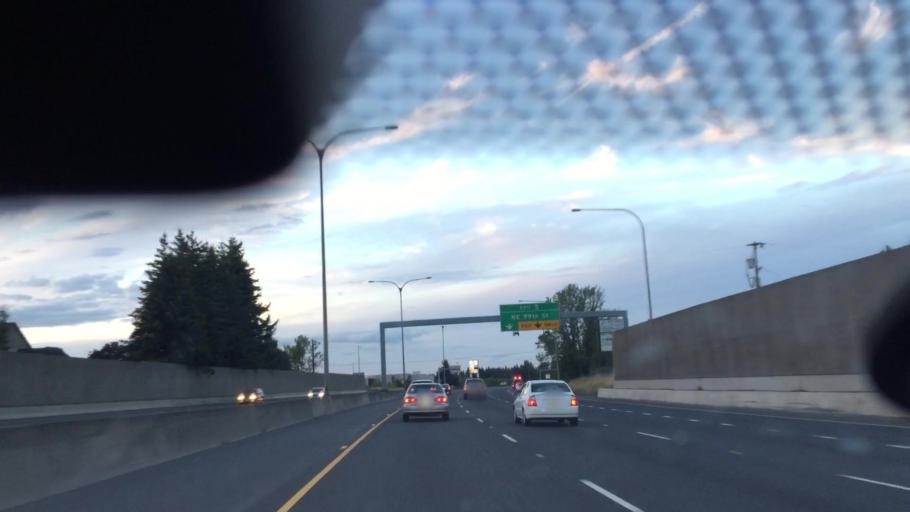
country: US
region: Washington
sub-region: Clark County
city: Hazel Dell
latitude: 45.6842
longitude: -122.6643
